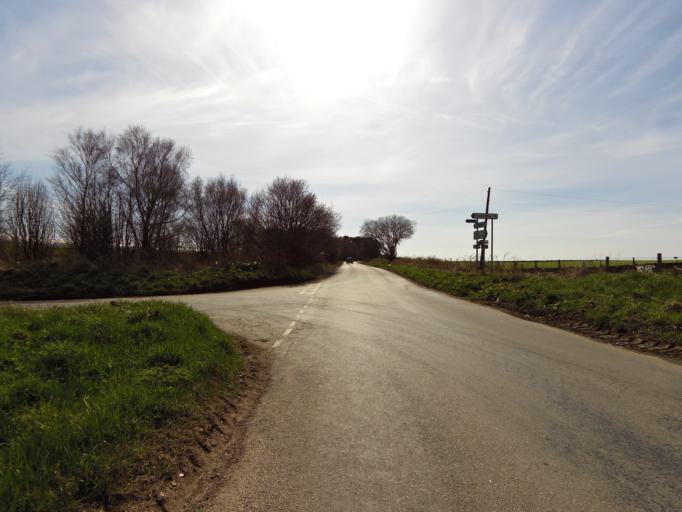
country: GB
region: Scotland
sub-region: Angus
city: Arbroath
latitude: 56.5814
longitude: -2.5568
